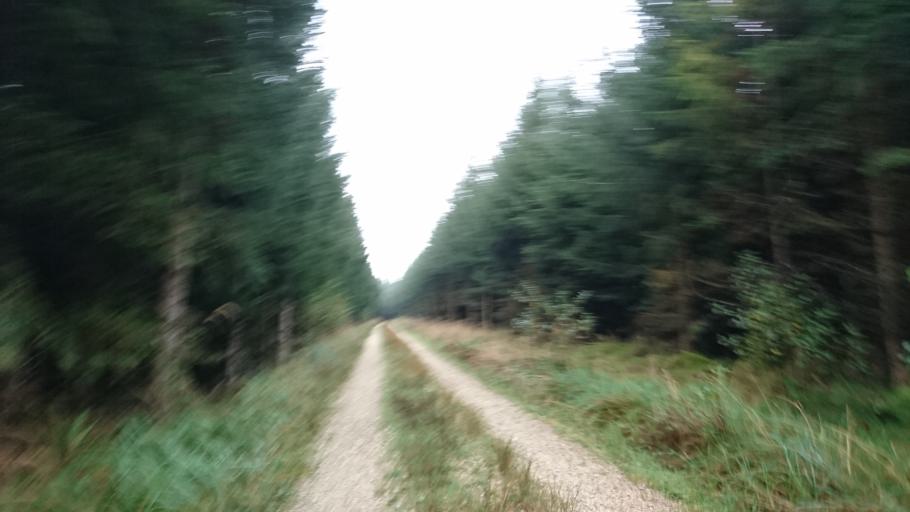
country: DE
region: Bavaria
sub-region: Swabia
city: Welden
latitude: 48.4348
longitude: 10.6369
